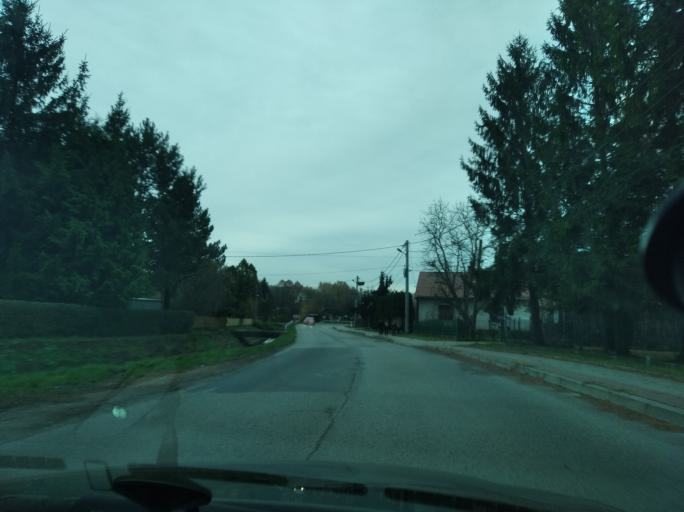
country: PL
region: Subcarpathian Voivodeship
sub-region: Powiat lancucki
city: Krzemienica
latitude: 50.0796
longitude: 22.1900
